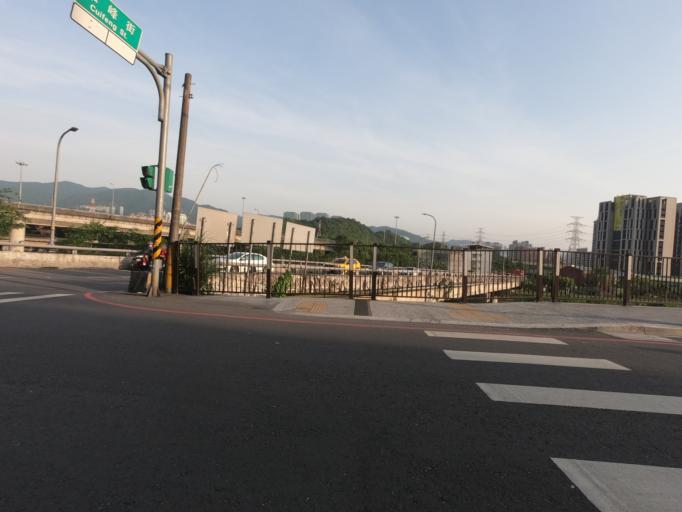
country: TW
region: Taiwan
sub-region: Keelung
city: Keelung
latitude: 25.0759
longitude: 121.6448
